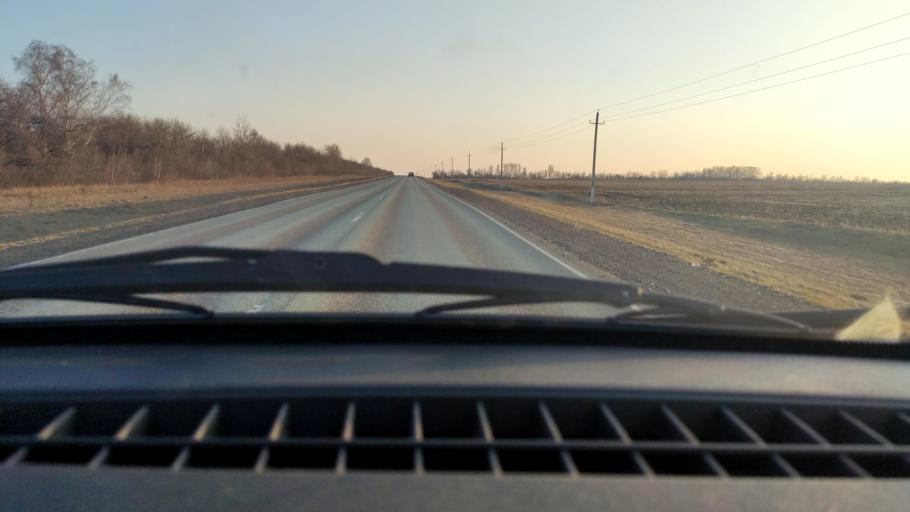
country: RU
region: Bashkortostan
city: Davlekanovo
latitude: 54.3239
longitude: 55.1597
